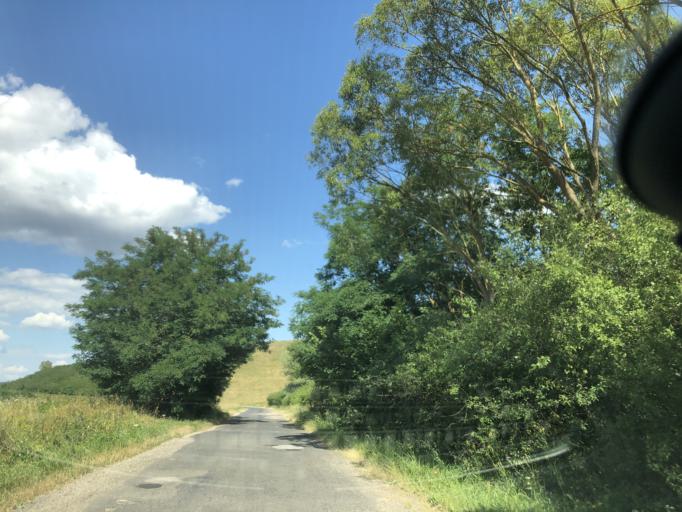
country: HU
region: Borsod-Abauj-Zemplen
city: Szendro
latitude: 48.5426
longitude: 20.7953
